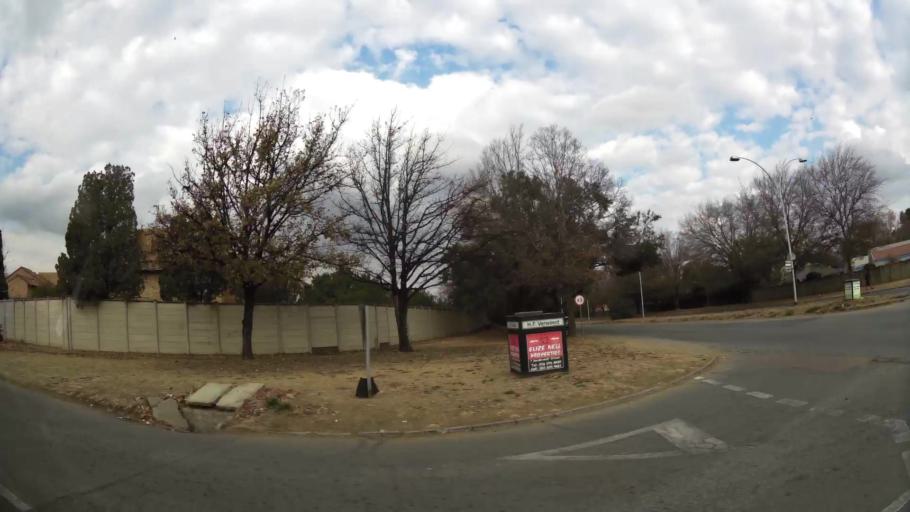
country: ZA
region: Orange Free State
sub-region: Fezile Dabi District Municipality
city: Sasolburg
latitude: -26.7993
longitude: 27.8085
